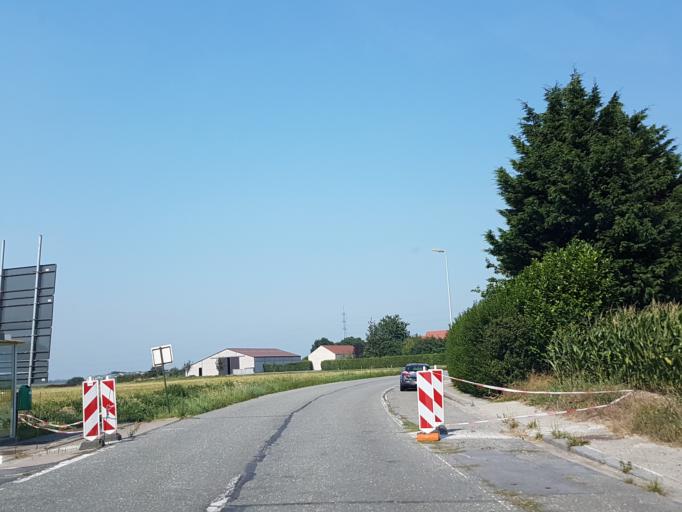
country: BE
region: Flanders
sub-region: Provincie West-Vlaanderen
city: Jabbeke
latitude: 51.2192
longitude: 3.0670
